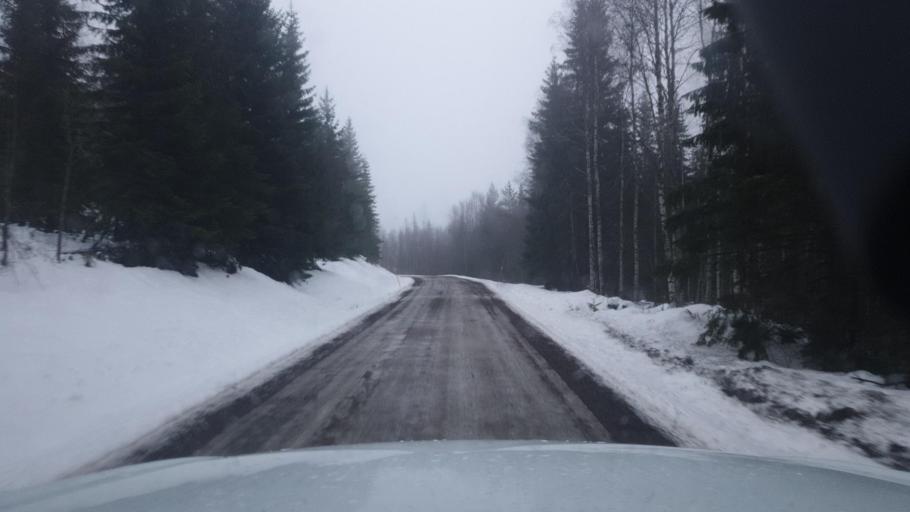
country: SE
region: Vaermland
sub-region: Eda Kommun
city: Charlottenberg
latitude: 60.0986
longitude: 12.6101
